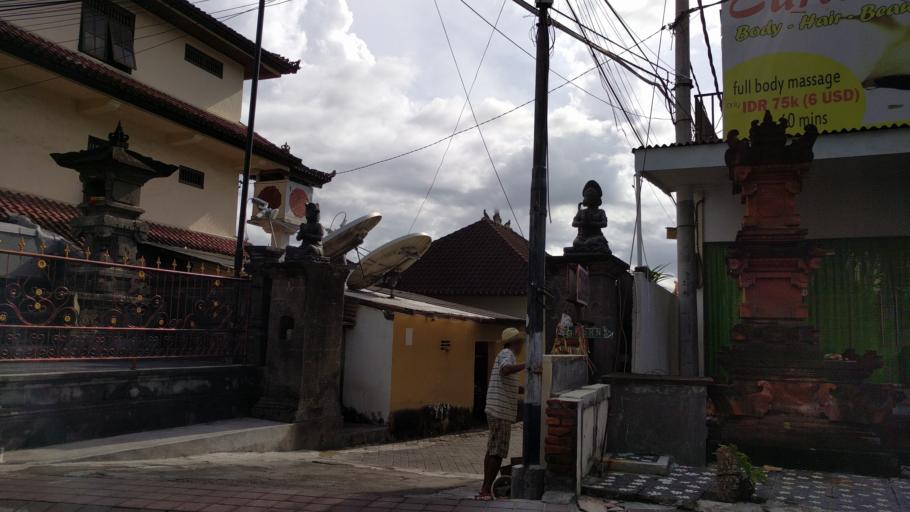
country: ID
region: Bali
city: Kuta
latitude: -8.6839
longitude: 115.1536
